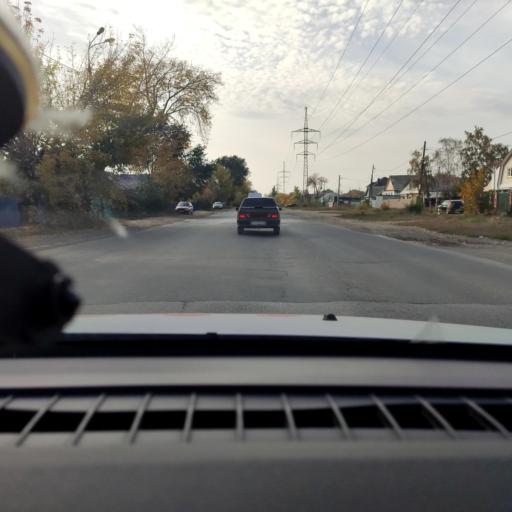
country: RU
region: Samara
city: Samara
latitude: 53.1329
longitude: 50.1310
